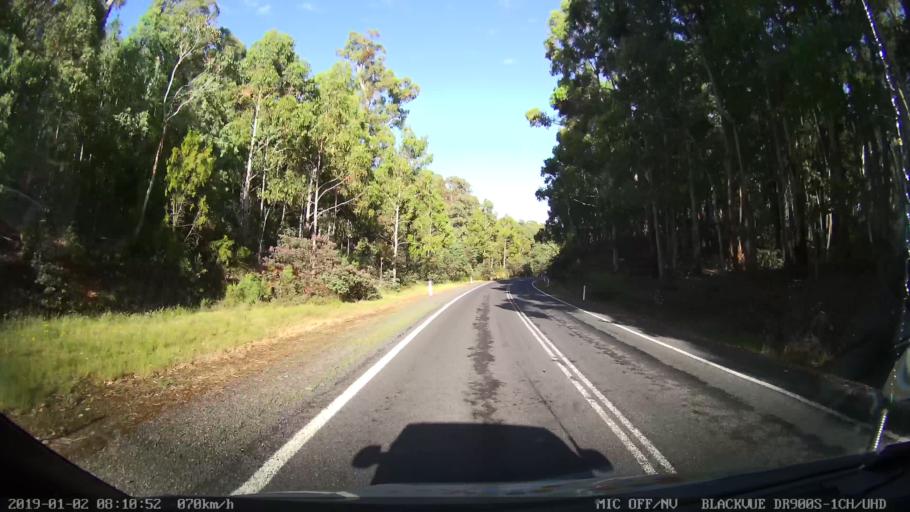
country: AU
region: New South Wales
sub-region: Tumut Shire
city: Tumut
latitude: -35.5987
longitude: 148.3646
